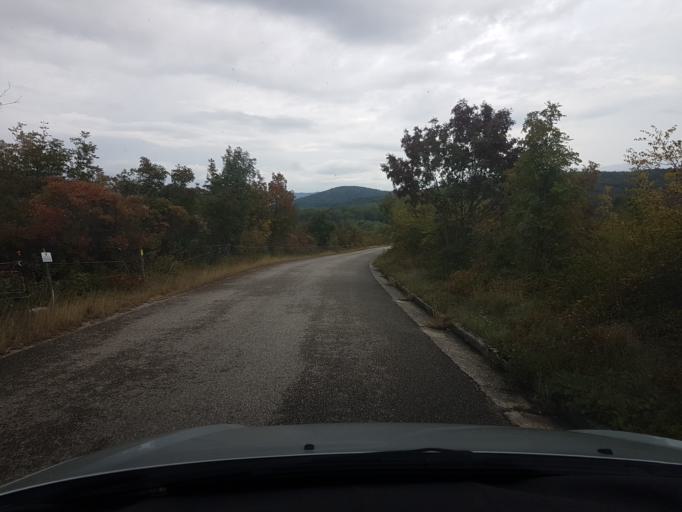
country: IT
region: Friuli Venezia Giulia
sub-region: Provincia di Gorizia
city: Doberdo del Lago
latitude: 45.8373
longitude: 13.5455
